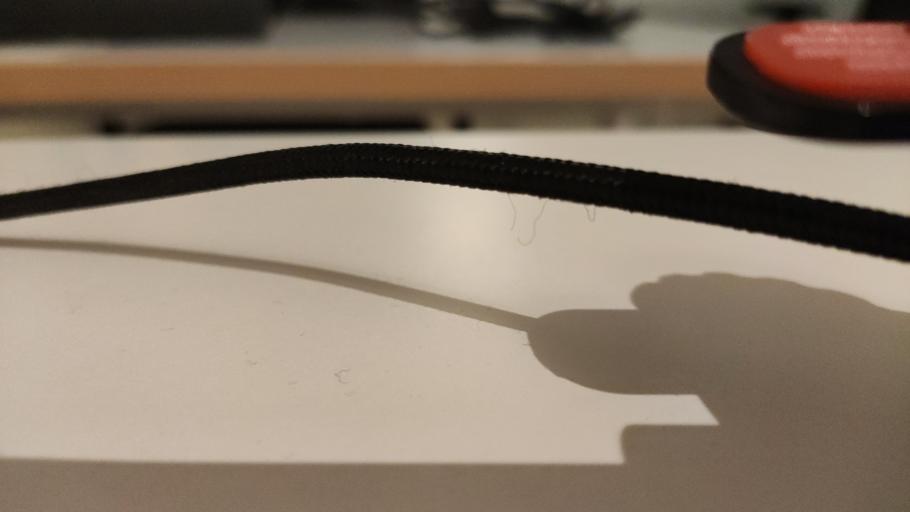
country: RU
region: Moskovskaya
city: Likino-Dulevo
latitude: 55.6981
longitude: 38.9552
